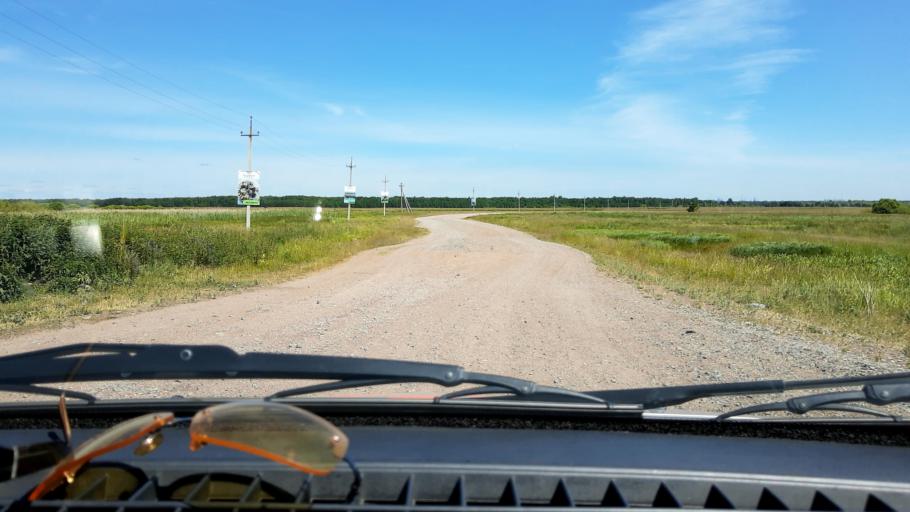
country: RU
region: Bashkortostan
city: Mikhaylovka
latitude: 54.9714
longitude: 55.7887
